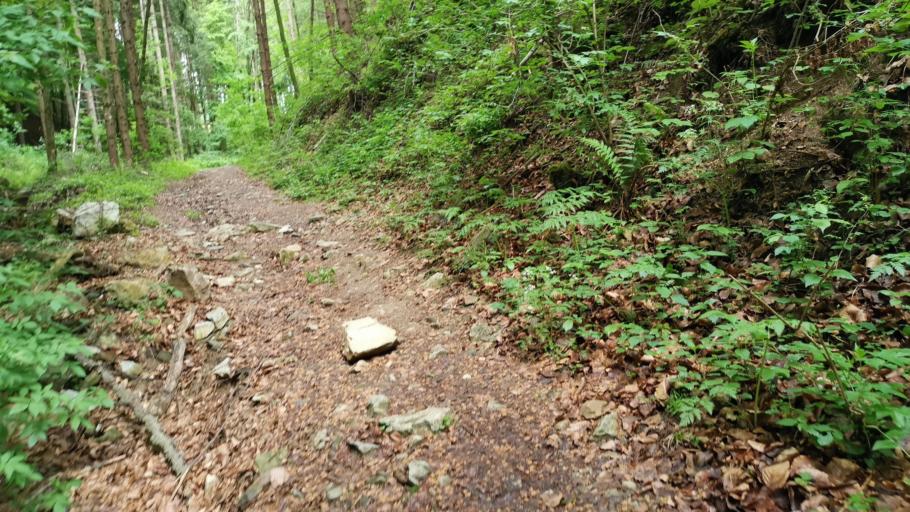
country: AT
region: Styria
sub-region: Politischer Bezirk Weiz
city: Mortantsch
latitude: 47.2329
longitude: 15.5600
